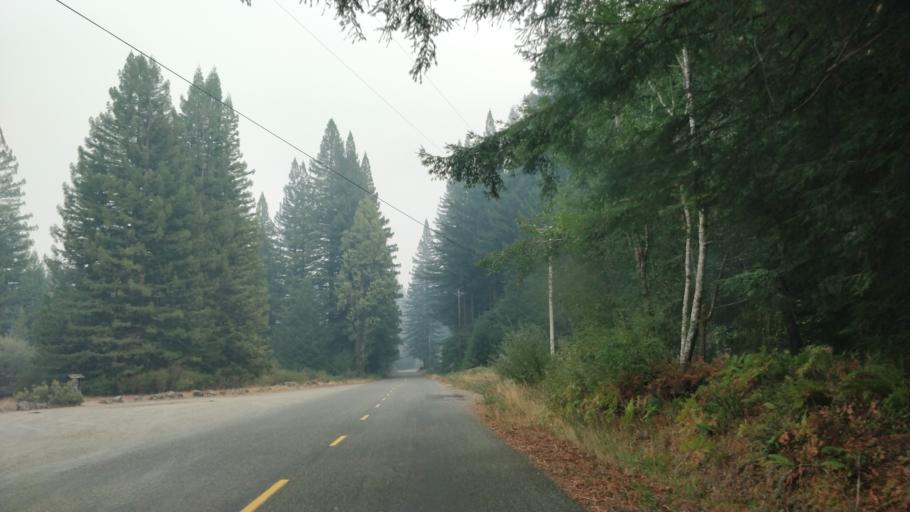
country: US
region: California
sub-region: Humboldt County
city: Rio Dell
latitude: 40.3506
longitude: -124.0159
